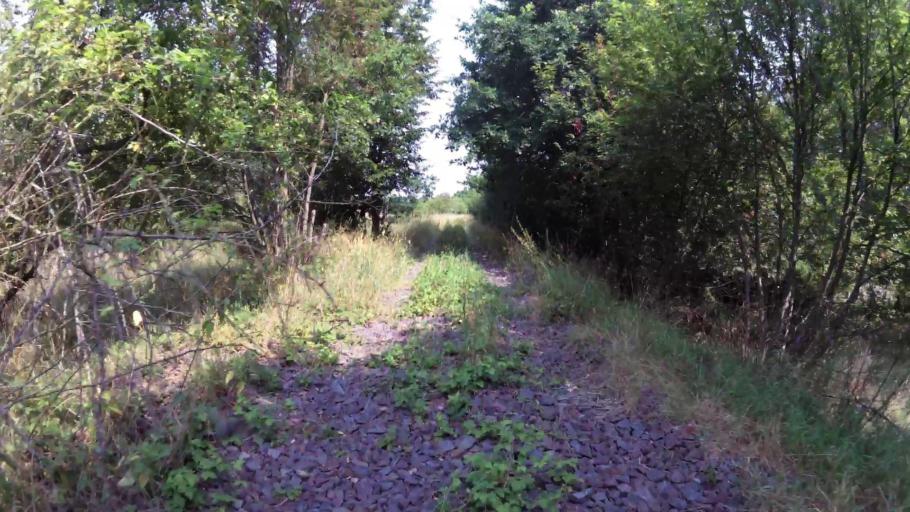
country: PL
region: West Pomeranian Voivodeship
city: Trzcinsko Zdroj
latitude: 52.9218
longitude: 14.5517
